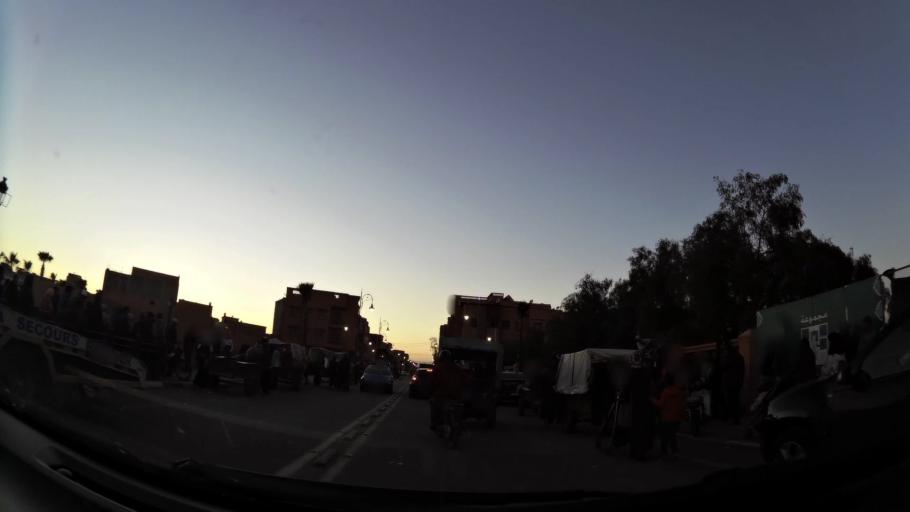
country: MA
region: Marrakech-Tensift-Al Haouz
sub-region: Kelaa-Des-Sraghna
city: Sidi Bou Othmane
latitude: 32.2276
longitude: -7.9455
